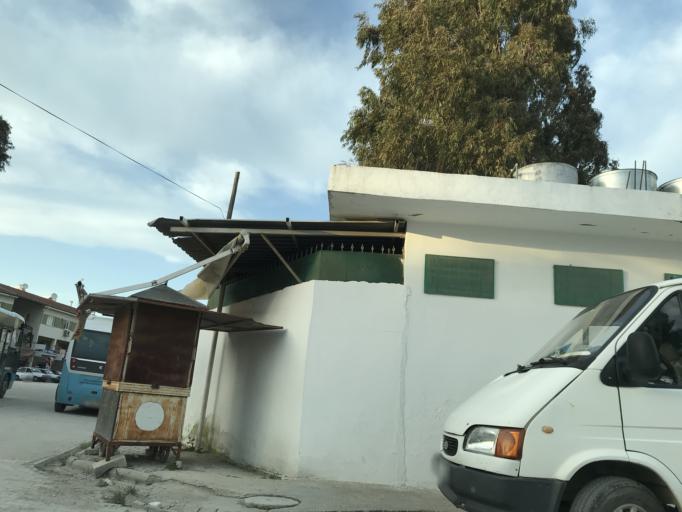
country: TR
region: Hatay
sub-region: Antakya Ilcesi
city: Antakya
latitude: 36.2121
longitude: 36.1657
